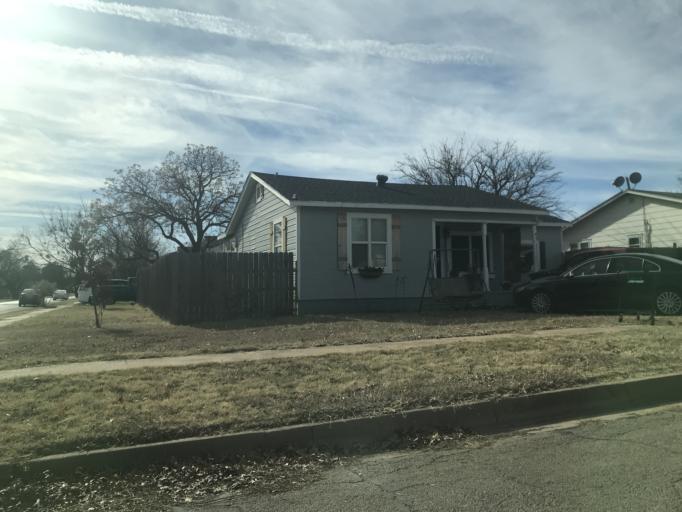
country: US
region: Texas
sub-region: Taylor County
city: Abilene
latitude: 32.4443
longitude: -99.7437
